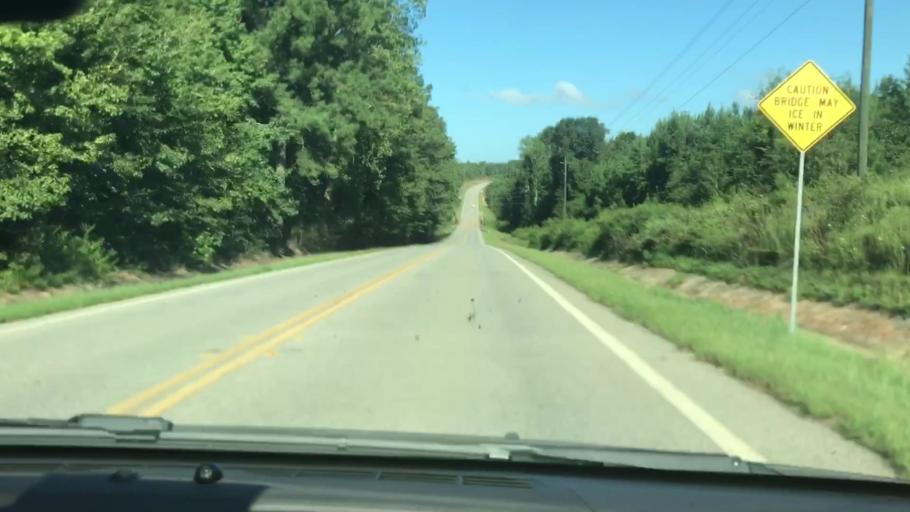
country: US
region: Georgia
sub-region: Quitman County
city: Georgetown
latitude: 31.7637
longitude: -85.0815
